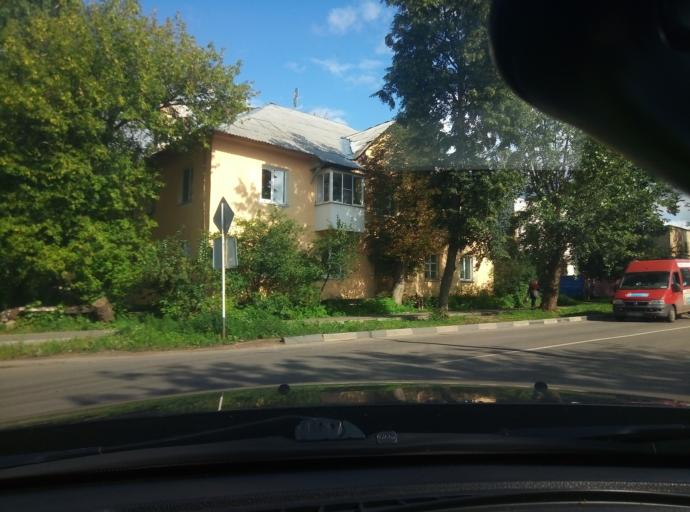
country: RU
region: Tula
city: Donskoy
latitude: 53.9699
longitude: 38.3314
